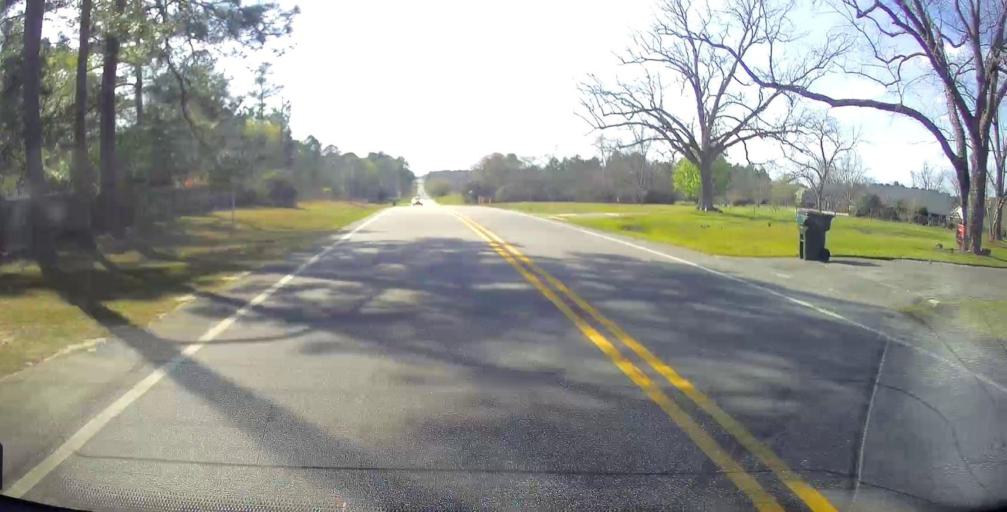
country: US
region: Georgia
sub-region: Dodge County
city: Eastman
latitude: 32.1963
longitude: -83.1875
